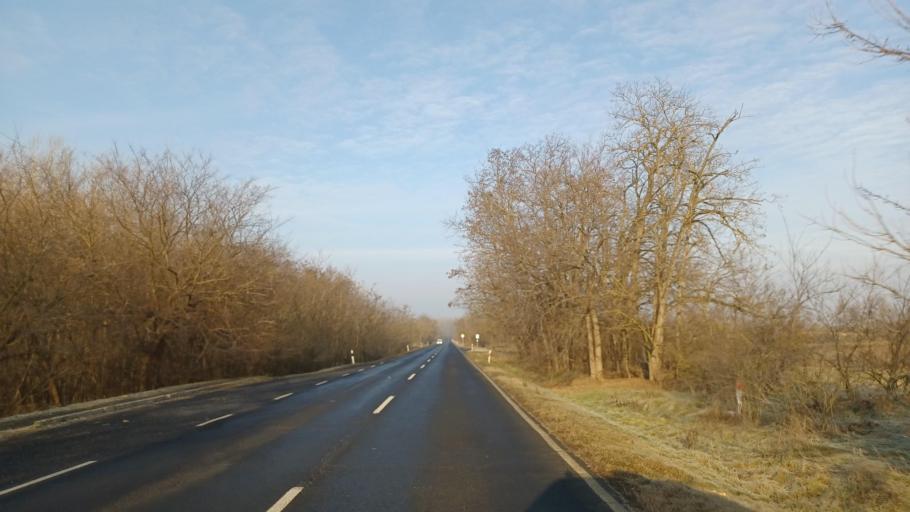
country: HU
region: Fejer
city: Cece
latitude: 46.7399
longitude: 18.6541
